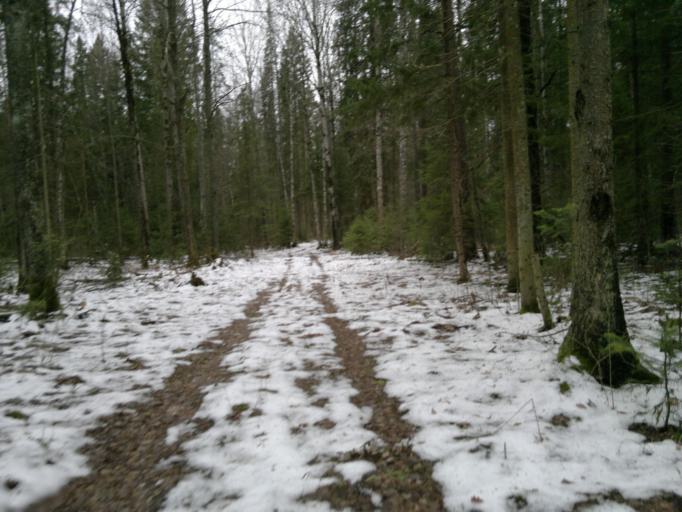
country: RU
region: Mariy-El
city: Yoshkar-Ola
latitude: 56.5938
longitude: 47.9692
